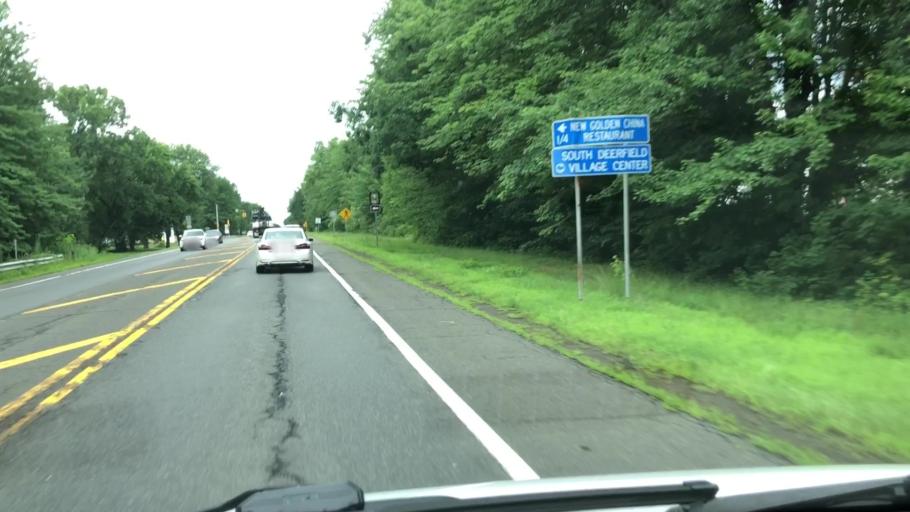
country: US
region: Massachusetts
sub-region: Franklin County
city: South Deerfield
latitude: 42.4794
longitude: -72.6132
